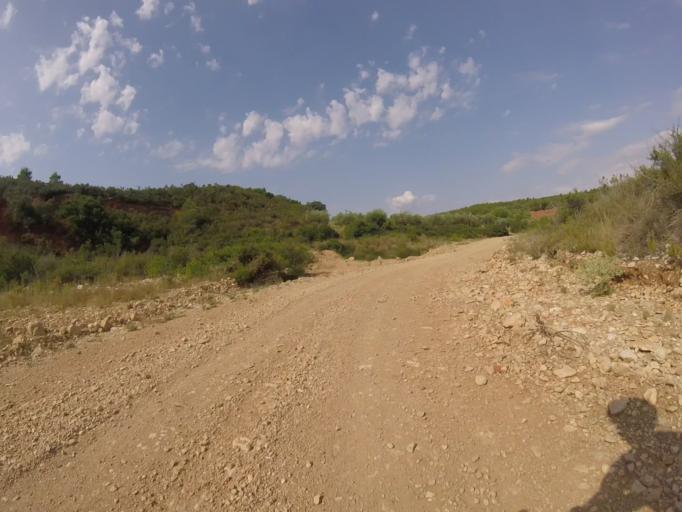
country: ES
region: Valencia
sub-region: Provincia de Castello
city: Alcala de Xivert
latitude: 40.3290
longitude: 0.1936
